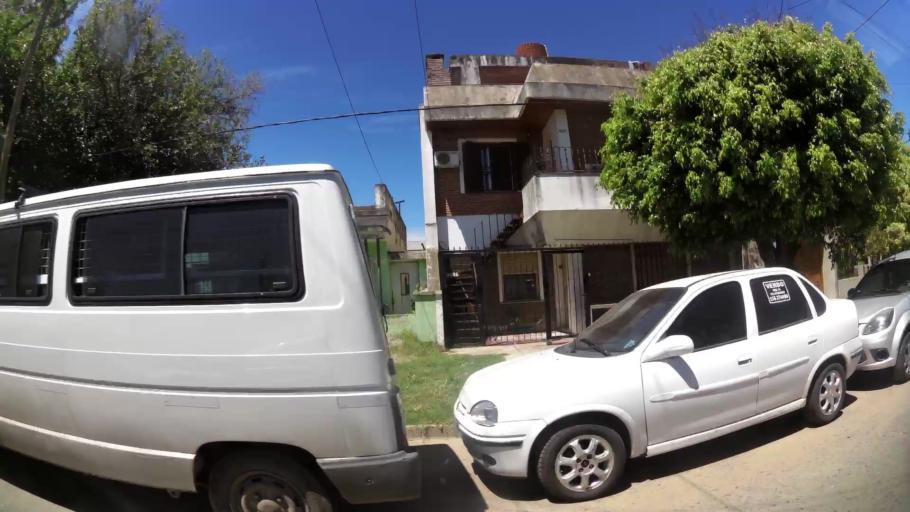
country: AR
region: Santa Fe
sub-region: Departamento de Rosario
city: Rosario
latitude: -32.9474
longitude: -60.7096
